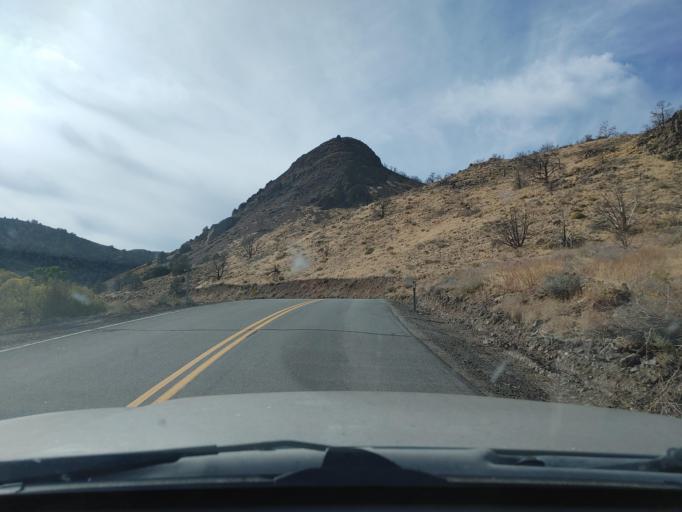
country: US
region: Nevada
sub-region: Storey County
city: Virginia City
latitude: 39.3099
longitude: -119.6012
